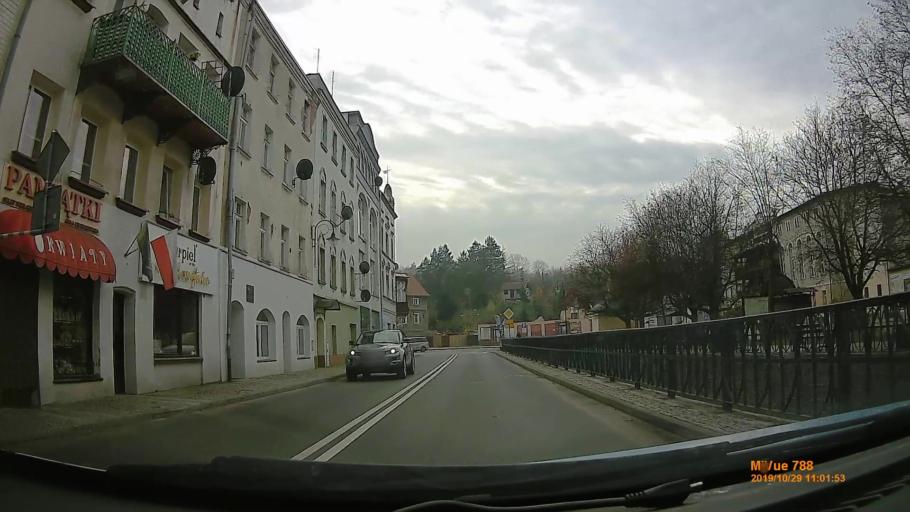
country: PL
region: Lower Silesian Voivodeship
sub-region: Powiat klodzki
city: Radkow
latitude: 50.4900
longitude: 16.4562
